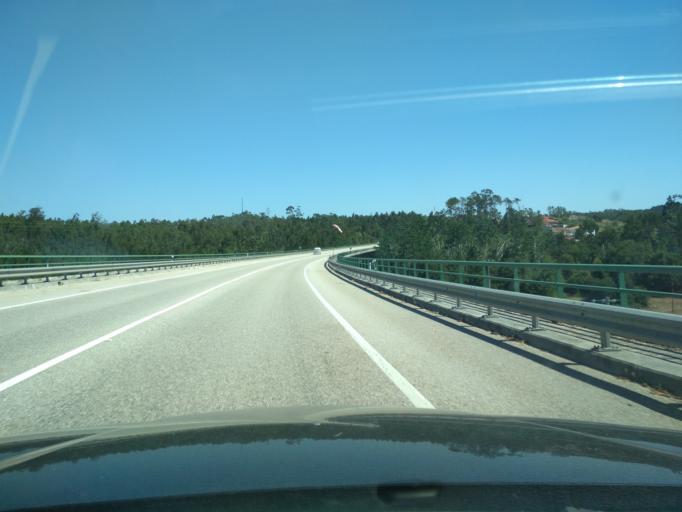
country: PT
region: Leiria
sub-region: Pombal
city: Lourical
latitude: 39.9882
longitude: -8.7394
